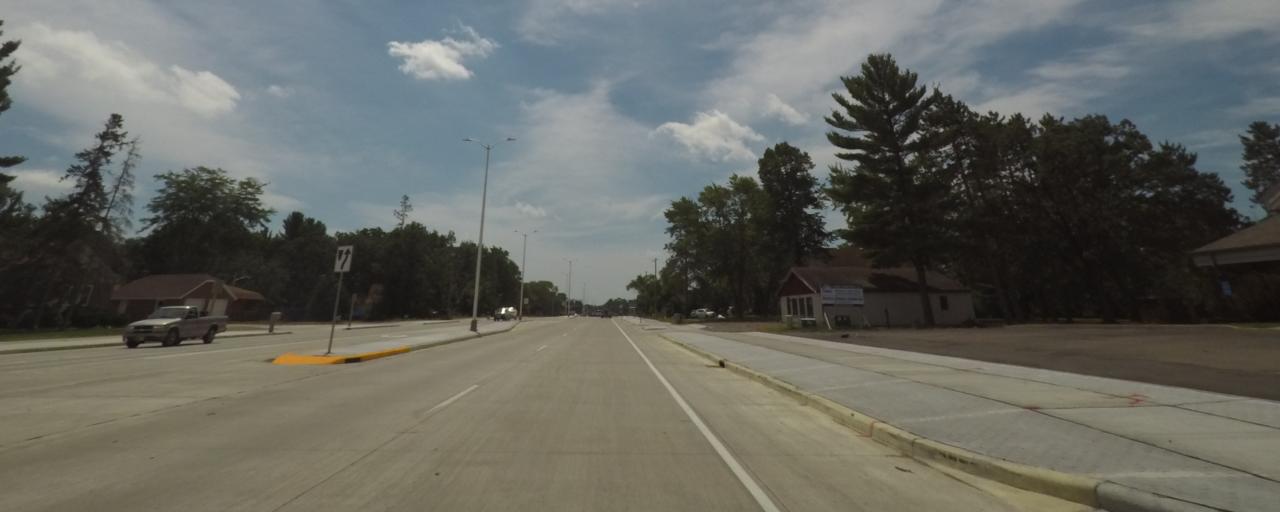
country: US
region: Wisconsin
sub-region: Portage County
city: Whiting
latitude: 44.4855
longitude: -89.5504
